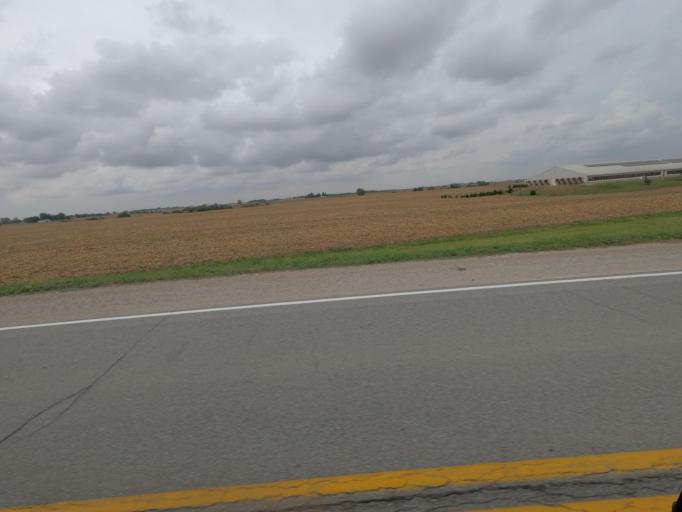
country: US
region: Iowa
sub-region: Wapello County
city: Ottumwa
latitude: 40.9501
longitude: -92.2298
